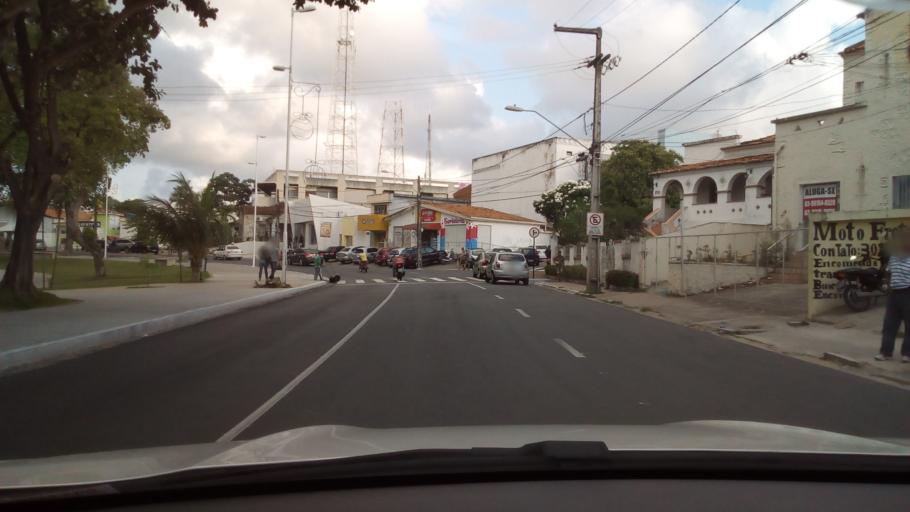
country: BR
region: Paraiba
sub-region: Joao Pessoa
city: Joao Pessoa
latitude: -7.1220
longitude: -34.8801
